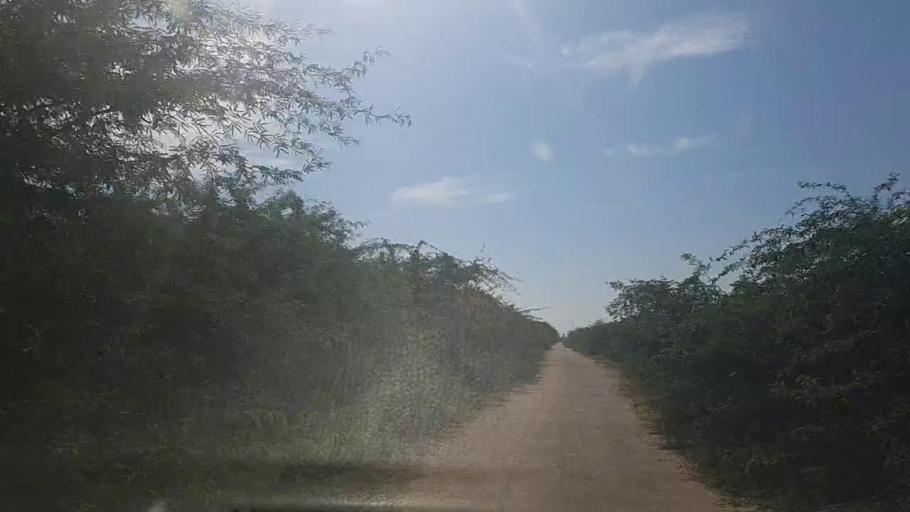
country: PK
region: Sindh
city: Mirpur Batoro
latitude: 24.6752
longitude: 68.1828
